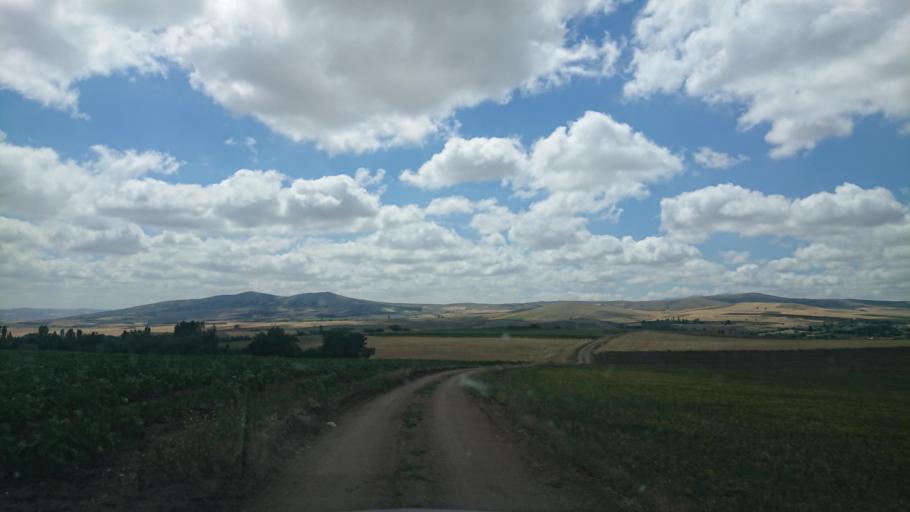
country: TR
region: Aksaray
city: Agacoren
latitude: 38.8313
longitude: 33.9515
